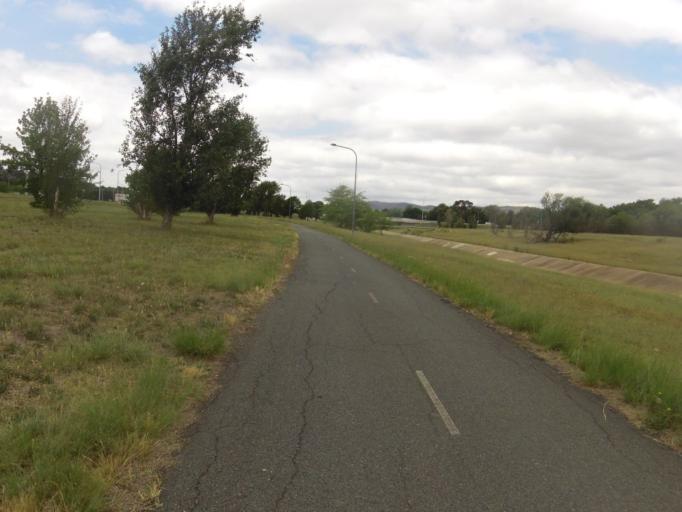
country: AU
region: Australian Capital Territory
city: Macarthur
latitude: -35.4217
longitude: 149.1007
